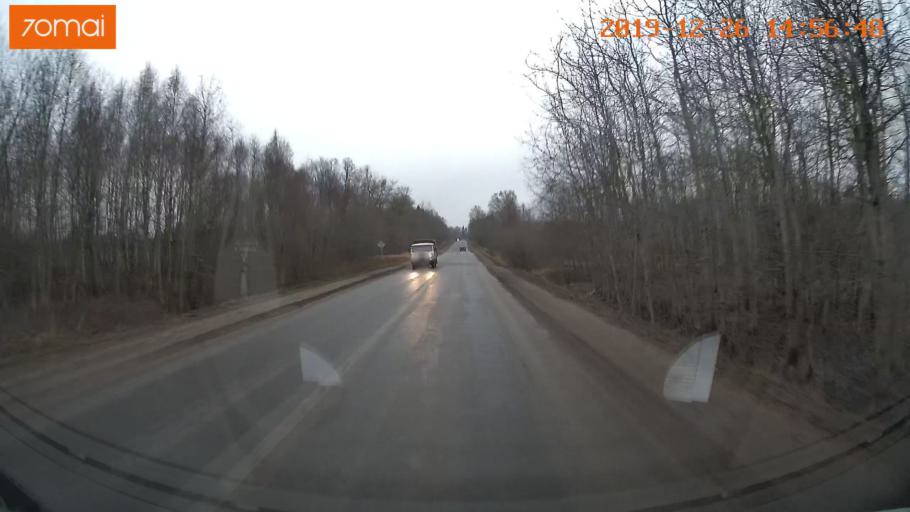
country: RU
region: Jaroslavl
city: Rybinsk
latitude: 58.2890
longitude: 38.8689
